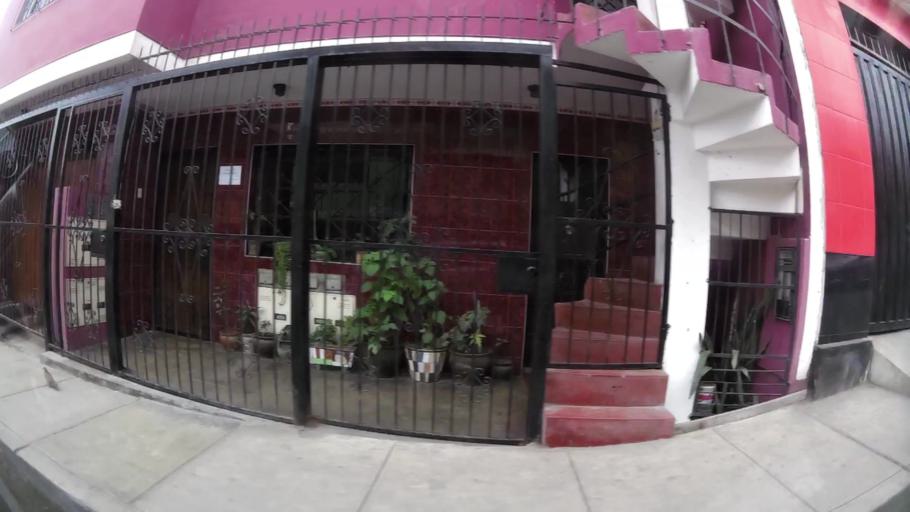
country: PE
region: Lima
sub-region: Lima
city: Surco
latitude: -12.1562
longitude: -76.9542
